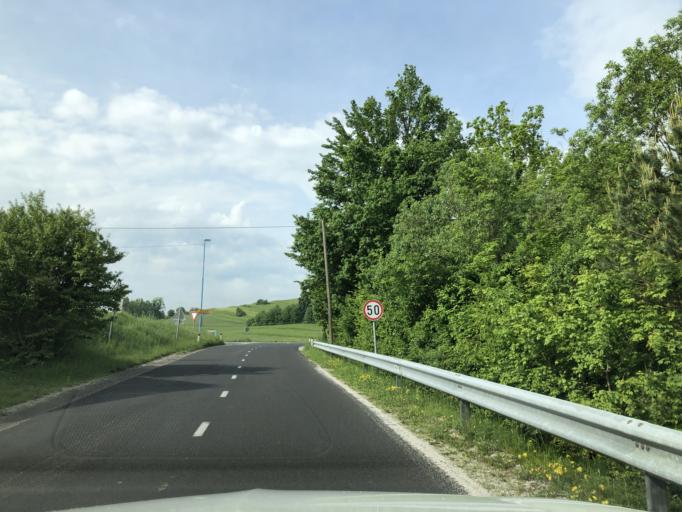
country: SI
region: Velike Lasce
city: Velike Lasce
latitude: 45.8154
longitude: 14.6260
